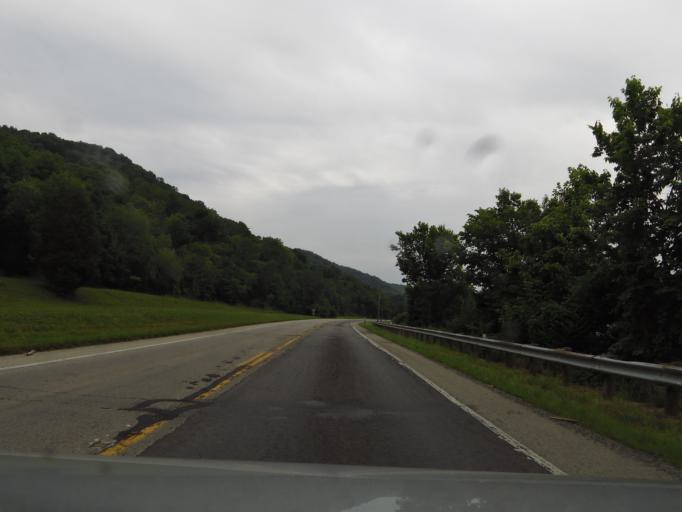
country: US
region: Ohio
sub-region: Brown County
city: Aberdeen
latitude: 38.7016
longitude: -83.7875
